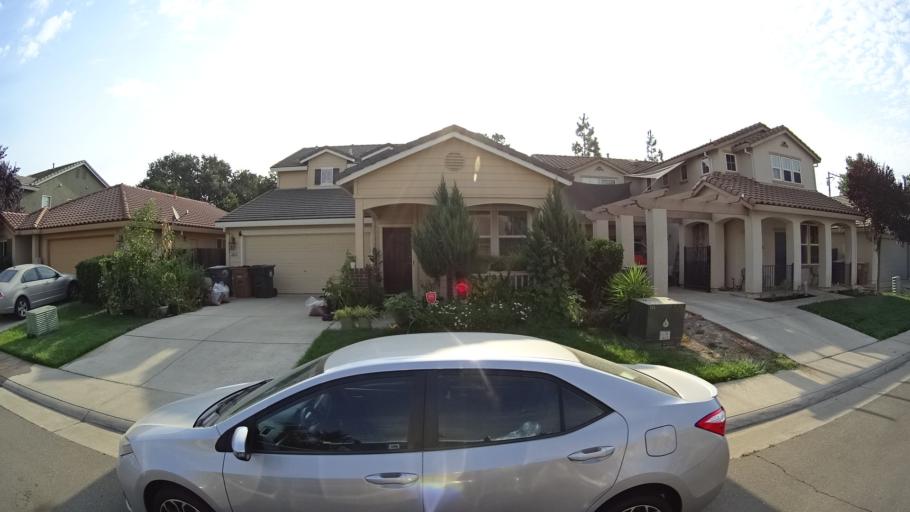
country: US
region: California
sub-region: Sacramento County
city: Laguna
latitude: 38.3910
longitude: -121.4181
